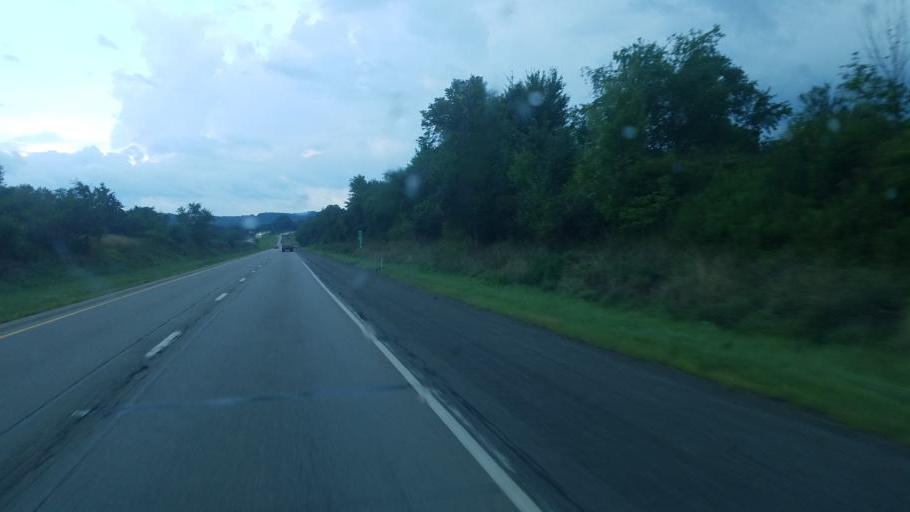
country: US
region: Pennsylvania
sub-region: Butler County
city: Slippery Rock
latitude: 41.0208
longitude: -80.1159
